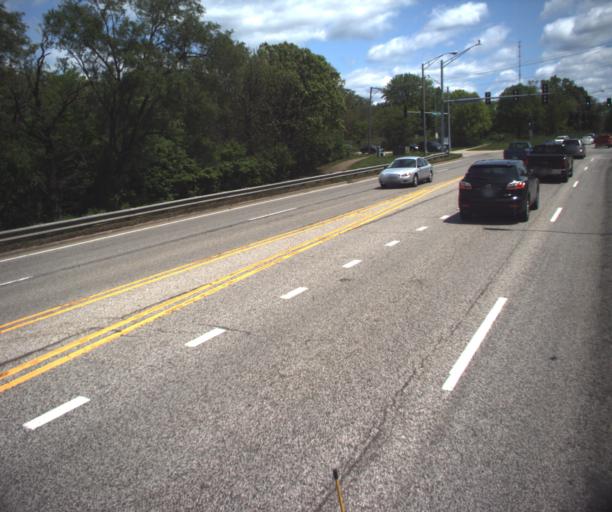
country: US
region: Illinois
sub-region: Kane County
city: Batavia
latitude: 41.8662
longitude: -88.3073
